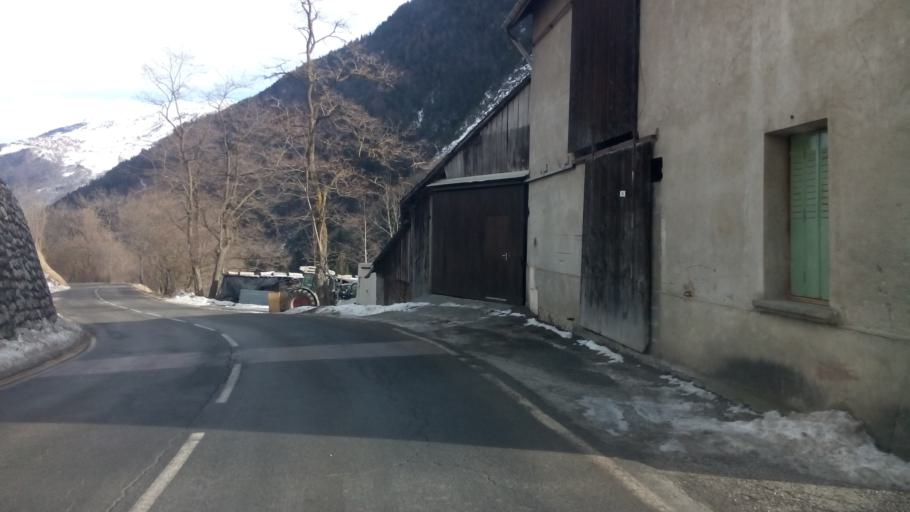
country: FR
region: Rhone-Alpes
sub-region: Departement de l'Isere
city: Huez
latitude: 45.0520
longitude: 5.9878
